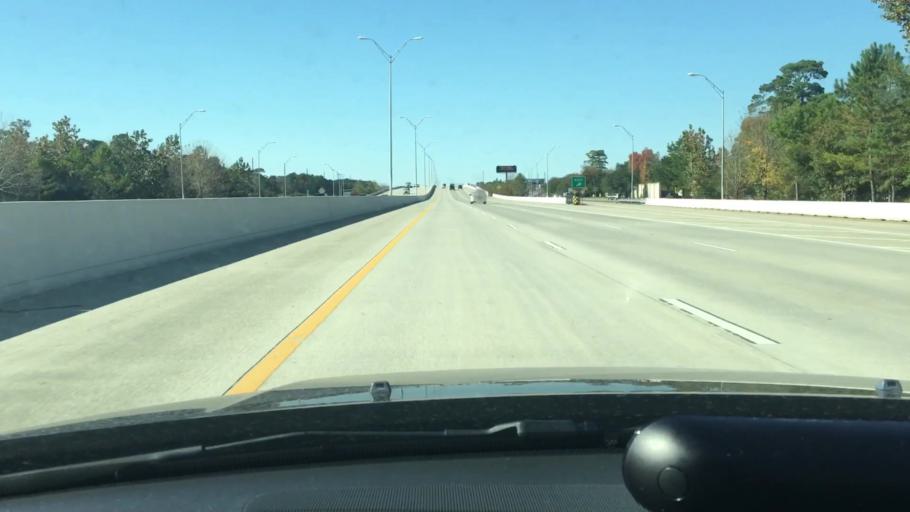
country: US
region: Texas
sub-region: Harris County
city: Humble
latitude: 29.9343
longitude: -95.2196
